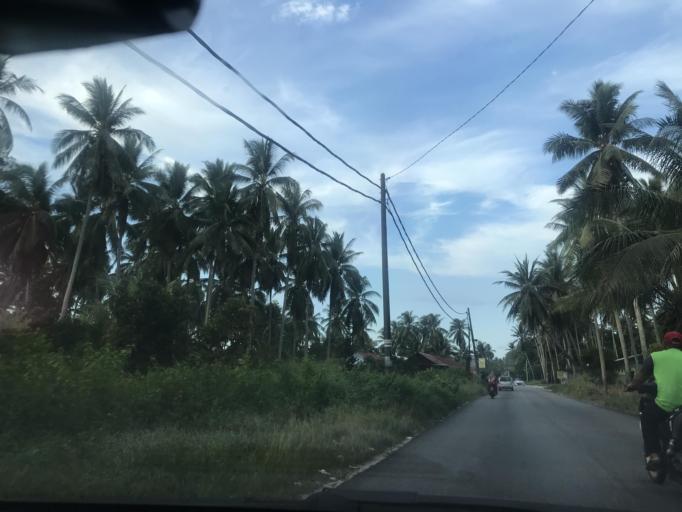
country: MY
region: Kelantan
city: Kota Bharu
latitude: 6.1261
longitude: 102.3561
